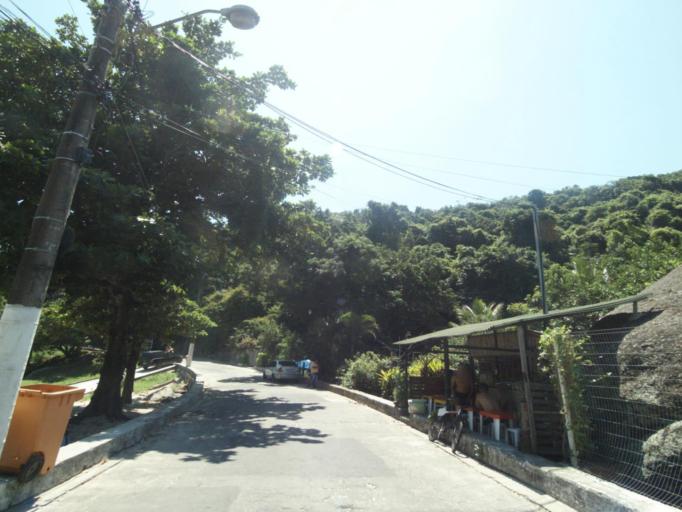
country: BR
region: Rio de Janeiro
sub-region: Niteroi
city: Niteroi
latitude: -22.9295
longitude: -43.1223
